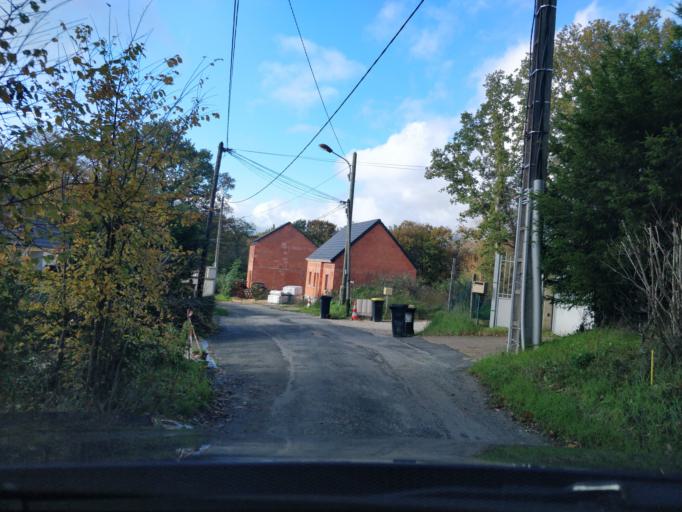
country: FR
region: Ile-de-France
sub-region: Departement de l'Essonne
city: Briis-sous-Forges
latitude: 48.6262
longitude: 2.1333
